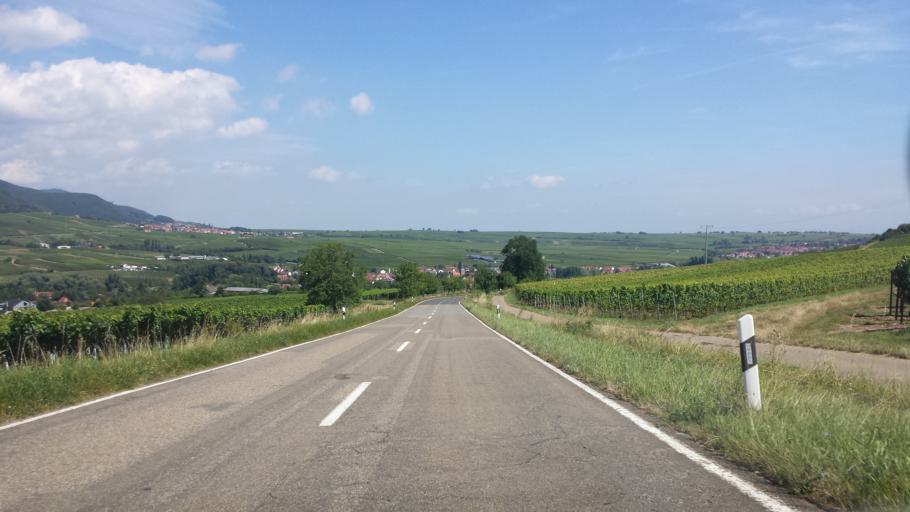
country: DE
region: Rheinland-Pfalz
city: Birkweiler
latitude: 49.2003
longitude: 8.0386
